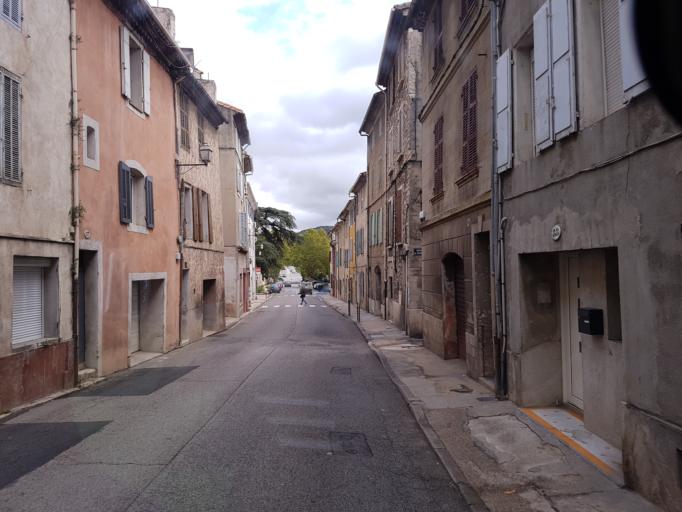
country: FR
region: Provence-Alpes-Cote d'Azur
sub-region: Departement des Bouches-du-Rhone
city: Cuges-les-Pins
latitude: 43.2758
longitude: 5.7028
